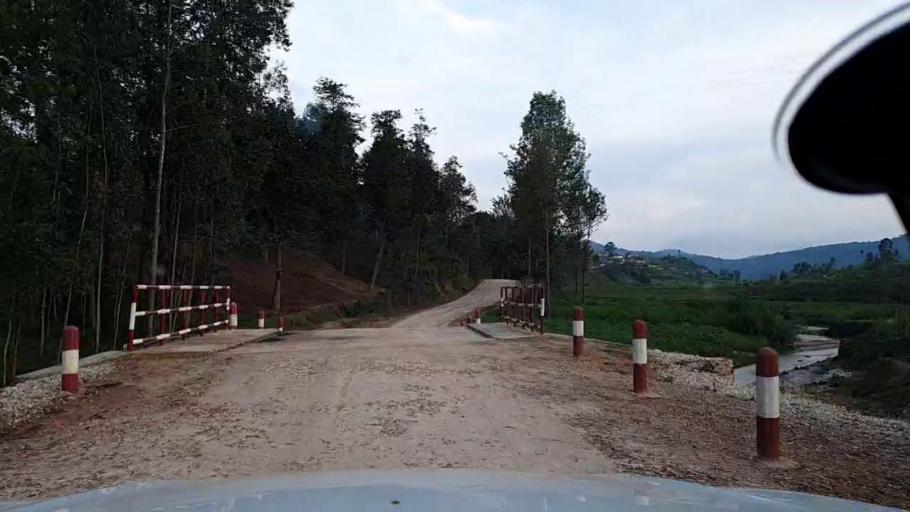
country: RW
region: Southern Province
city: Nyanza
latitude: -2.2165
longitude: 29.6428
